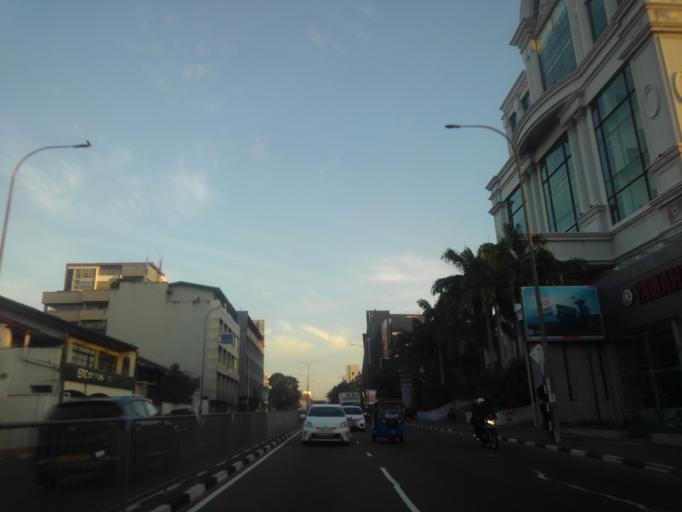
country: LK
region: Western
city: Kolonnawa
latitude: 6.9100
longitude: 79.8775
